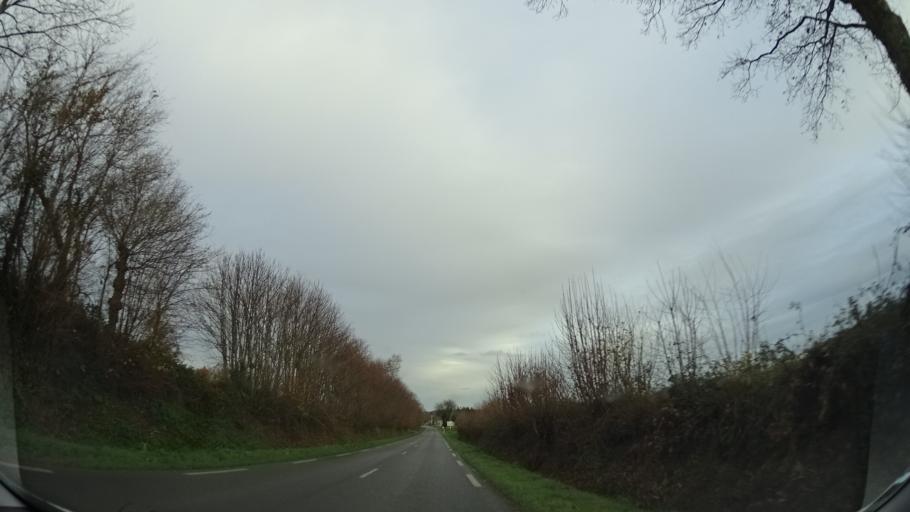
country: FR
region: Brittany
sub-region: Departement des Cotes-d'Armor
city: Evran
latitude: 48.3343
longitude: -1.9620
